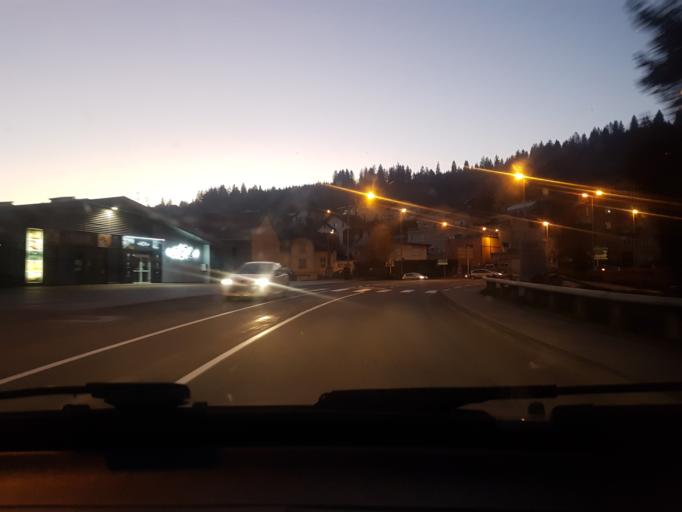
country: FR
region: Franche-Comte
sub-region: Departement du Doubs
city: Morteau
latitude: 47.0606
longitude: 6.6072
